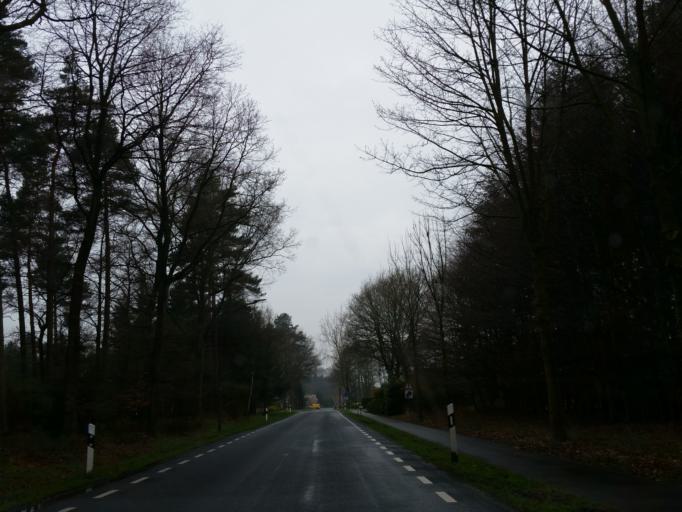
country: DE
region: Lower Saxony
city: Hipstedt
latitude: 53.5218
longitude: 8.9529
